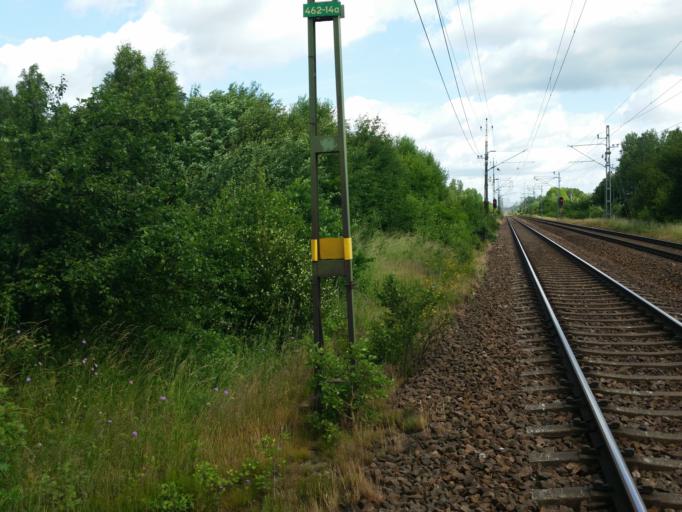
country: SE
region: Kronoberg
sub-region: Alvesta Kommun
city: Vislanda
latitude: 56.7013
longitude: 14.3300
